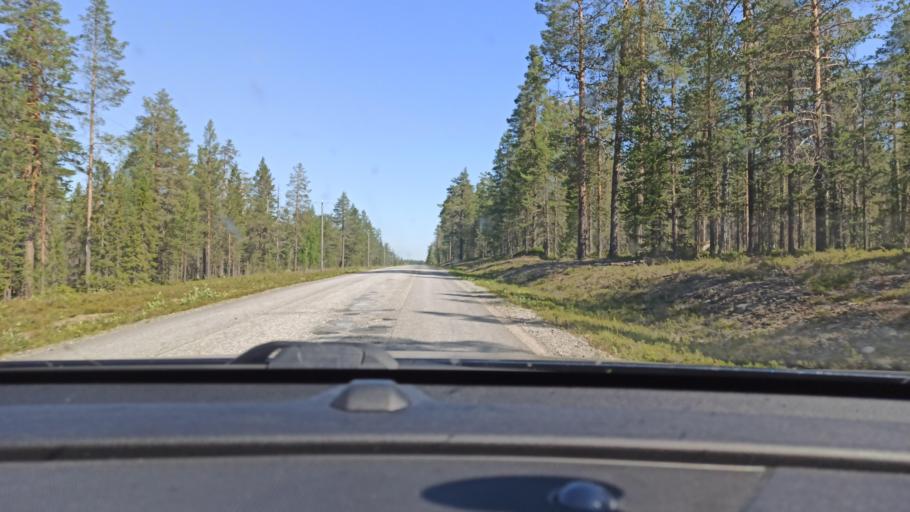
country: FI
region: Lapland
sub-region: Tunturi-Lappi
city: Kolari
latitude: 67.6401
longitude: 24.1576
